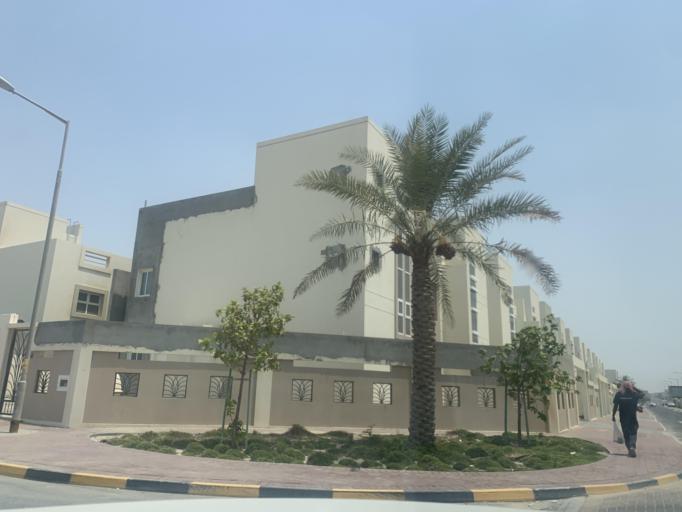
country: BH
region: Central Governorate
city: Madinat Hamad
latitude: 26.1362
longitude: 50.4667
